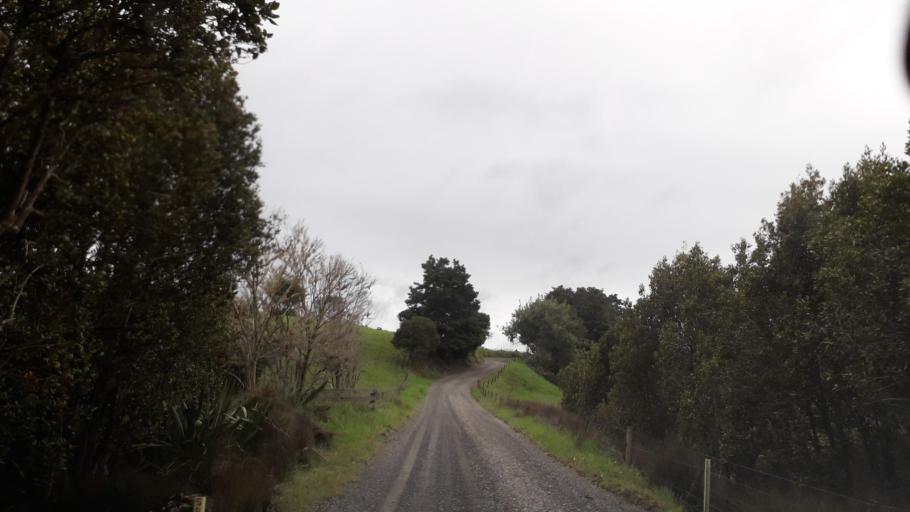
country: NZ
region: Northland
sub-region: Far North District
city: Waimate North
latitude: -35.3021
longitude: 173.5652
